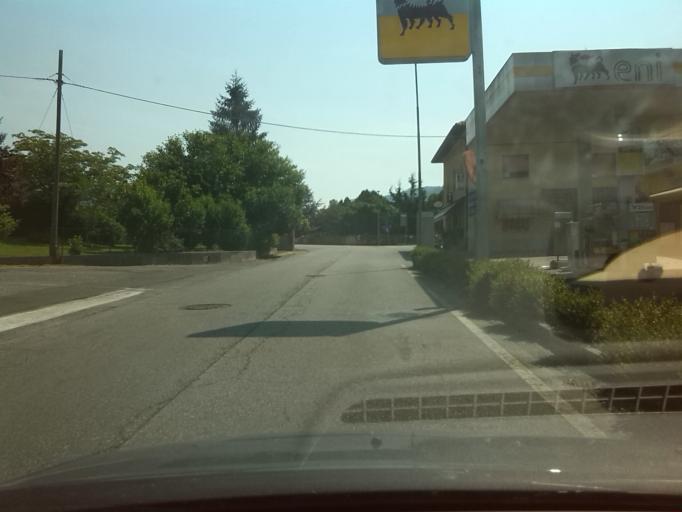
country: IT
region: Friuli Venezia Giulia
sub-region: Provincia di Udine
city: San Pietro al Natisone
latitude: 46.1155
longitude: 13.5050
